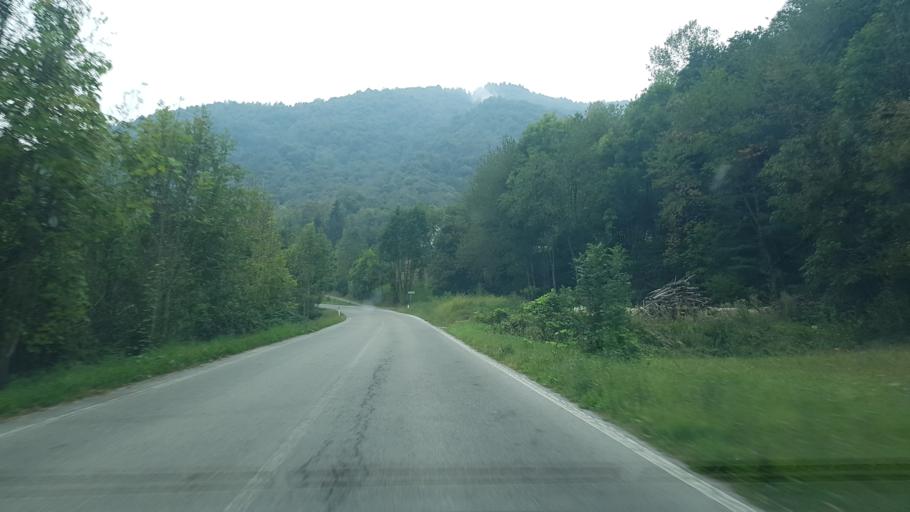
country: IT
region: Piedmont
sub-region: Provincia di Cuneo
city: Roccaforte Mondovi
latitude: 44.2876
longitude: 7.7450
